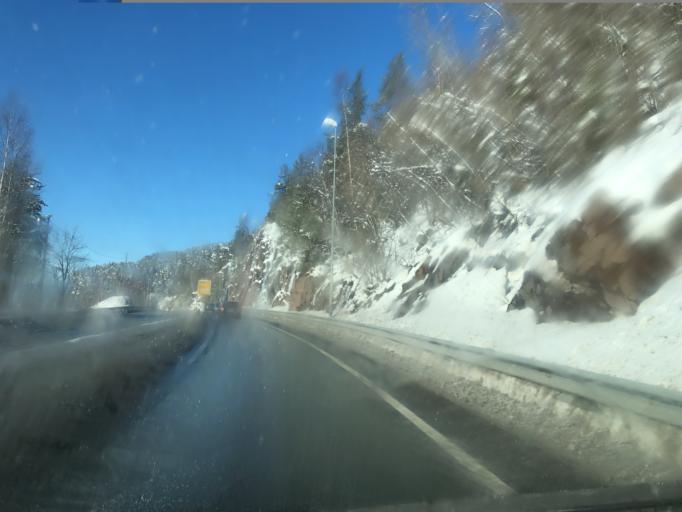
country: NO
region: Buskerud
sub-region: Hole
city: Vik
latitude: 59.9856
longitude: 10.3070
